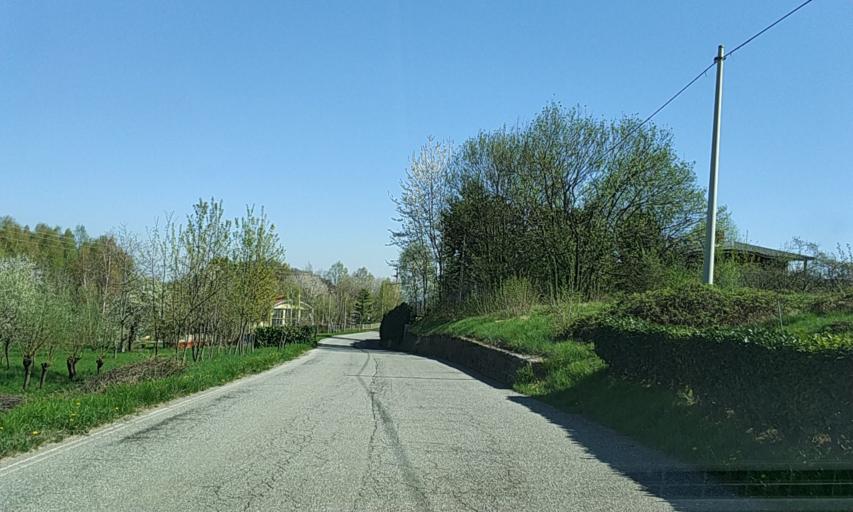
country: IT
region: Piedmont
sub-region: Provincia di Torino
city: Forno Canavese
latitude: 45.3379
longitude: 7.5912
